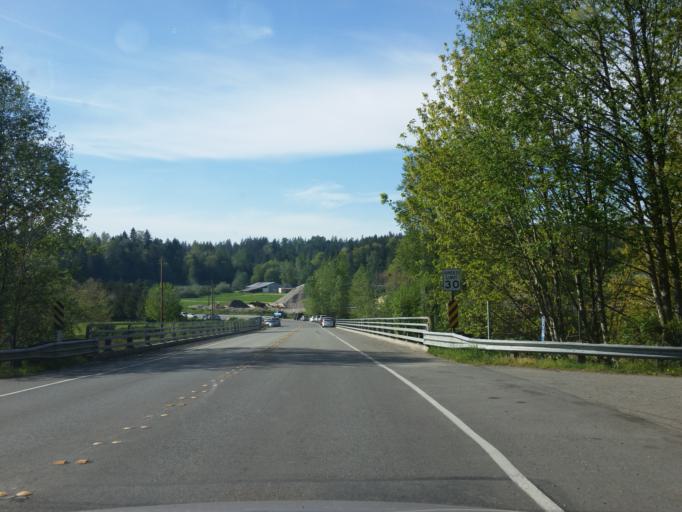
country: US
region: Washington
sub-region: Snohomish County
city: Machias
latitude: 47.9620
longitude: -122.0643
